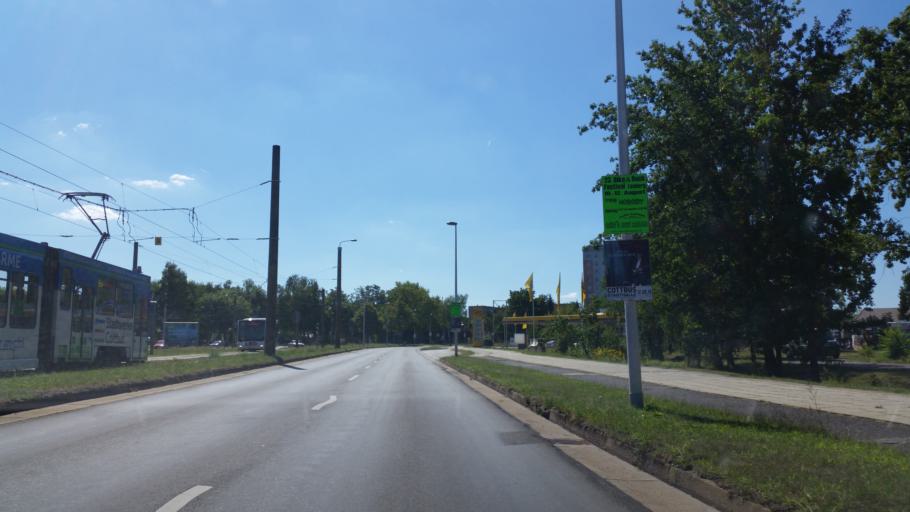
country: DE
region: Brandenburg
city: Cottbus
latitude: 51.7358
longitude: 14.3246
